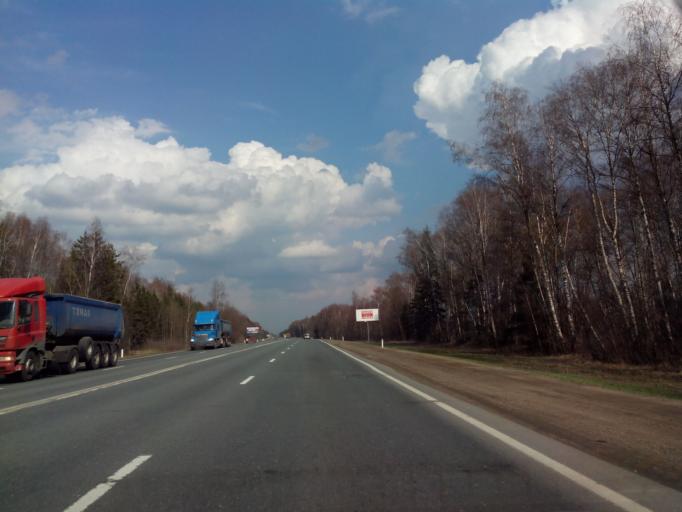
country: RU
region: Moskovskaya
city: Chupryakovo
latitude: 55.5587
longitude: 36.5802
